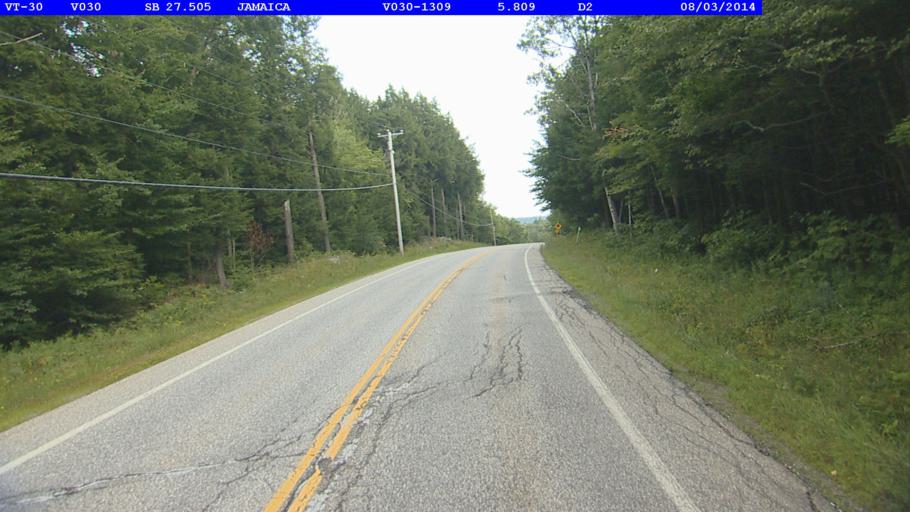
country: US
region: Vermont
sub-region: Windham County
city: Dover
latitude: 43.1163
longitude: -72.8035
